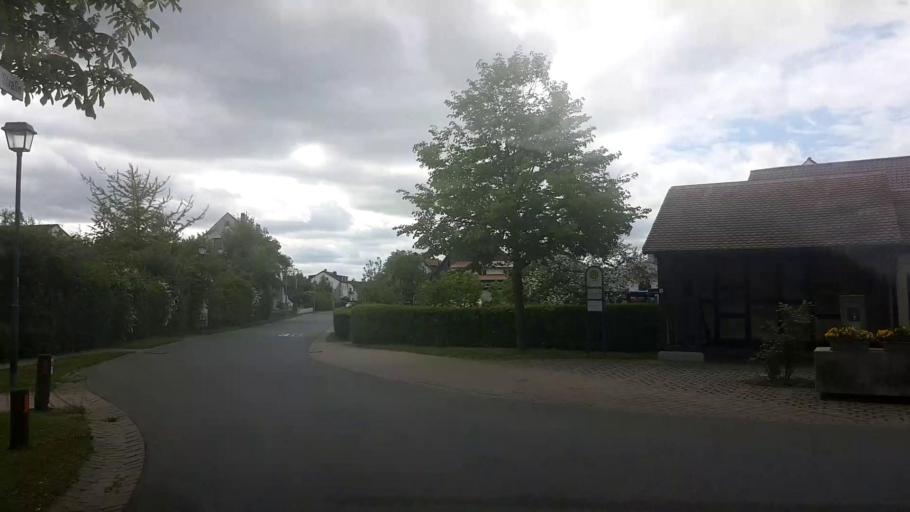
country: DE
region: Bavaria
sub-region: Upper Franconia
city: Lichtenfels
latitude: 50.1318
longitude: 11.0263
